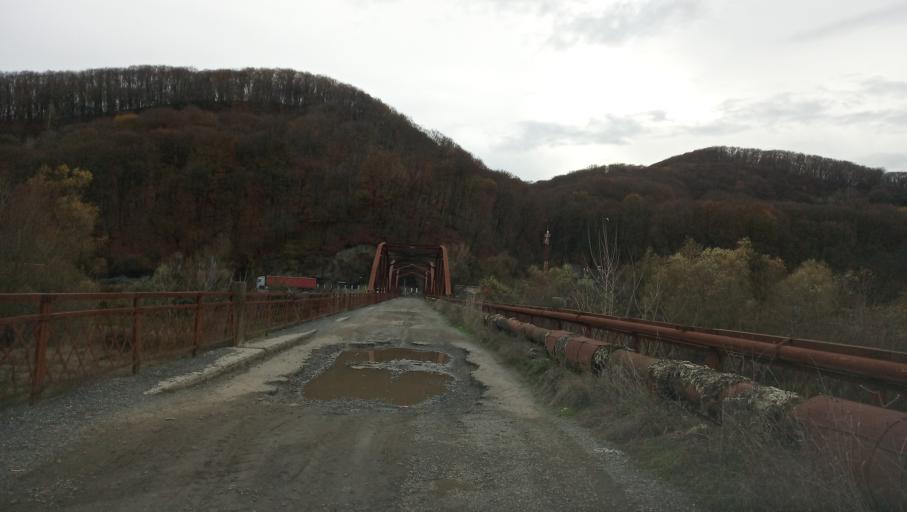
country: RO
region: Hunedoara
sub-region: Comuna Ilia
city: Ilia
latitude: 45.9231
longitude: 22.6633
